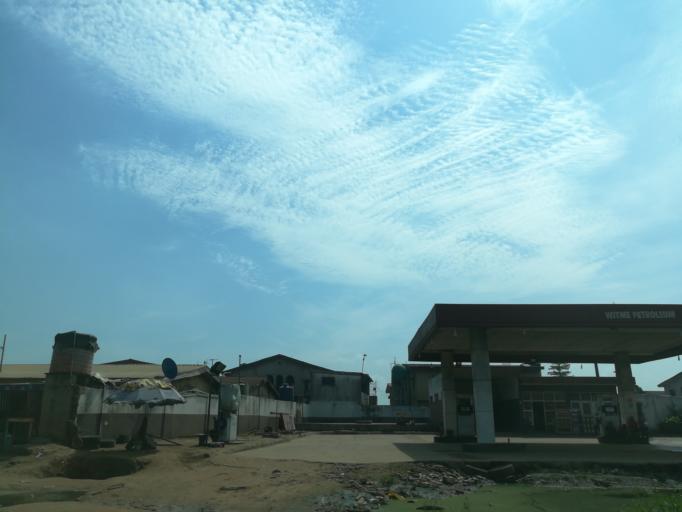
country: NG
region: Lagos
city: Ikorodu
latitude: 6.6361
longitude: 3.4822
